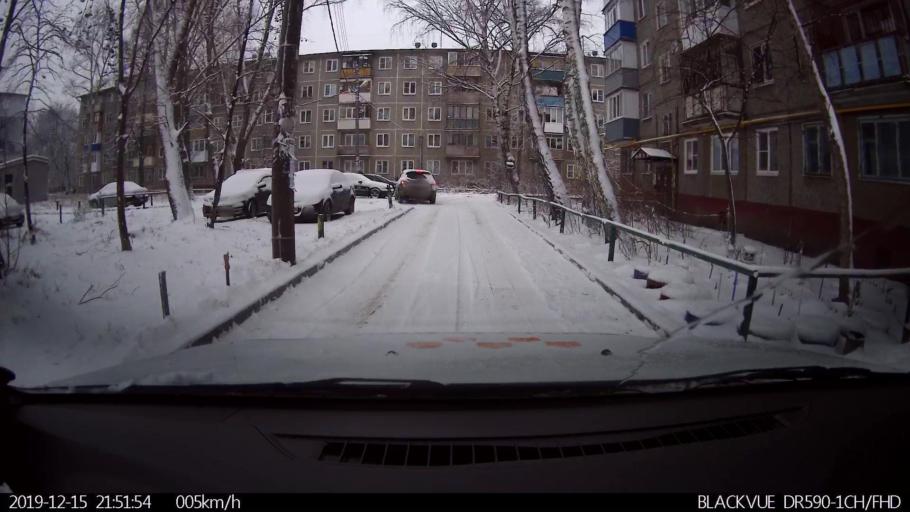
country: RU
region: Nizjnij Novgorod
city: Burevestnik
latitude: 56.2281
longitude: 43.8703
